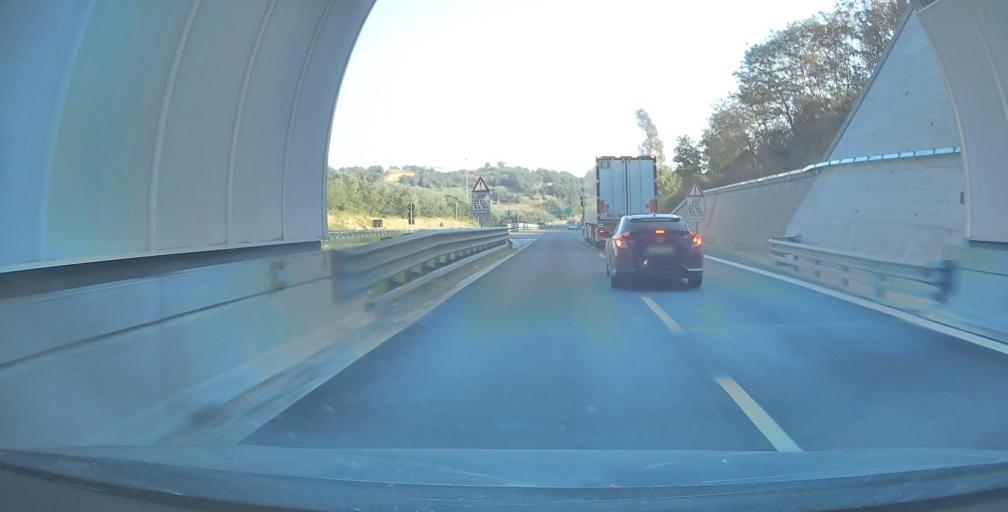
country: IT
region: Calabria
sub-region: Provincia di Cosenza
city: Rosario
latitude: 39.2954
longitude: 16.2377
